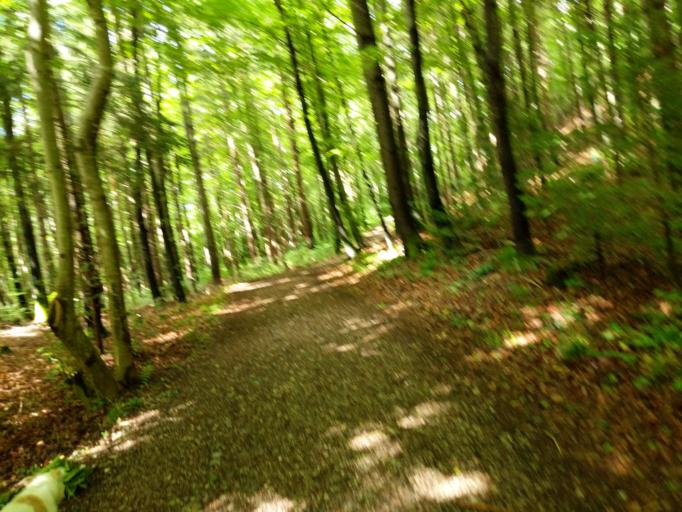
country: DE
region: Bavaria
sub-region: Upper Bavaria
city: Herrsching am Ammersee
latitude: 48.0103
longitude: 11.1897
